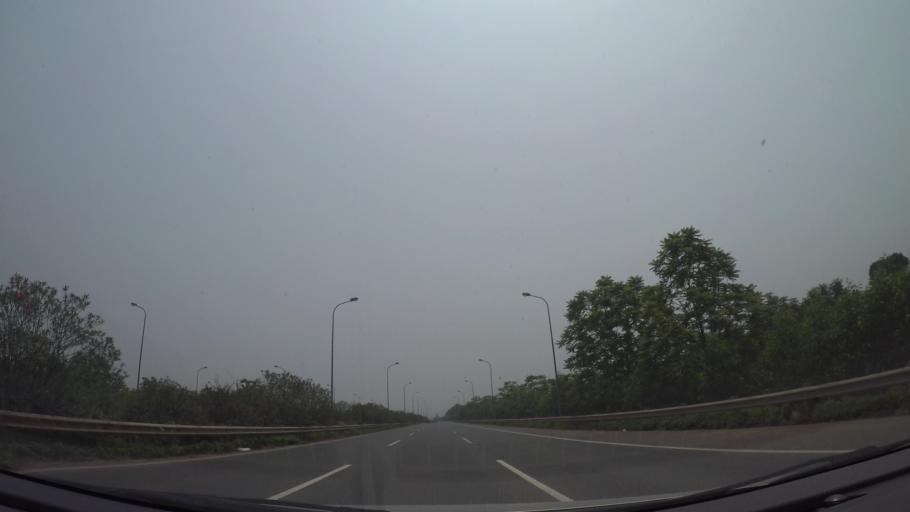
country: VN
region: Ha Noi
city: Lien Quan
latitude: 20.9892
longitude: 105.5677
